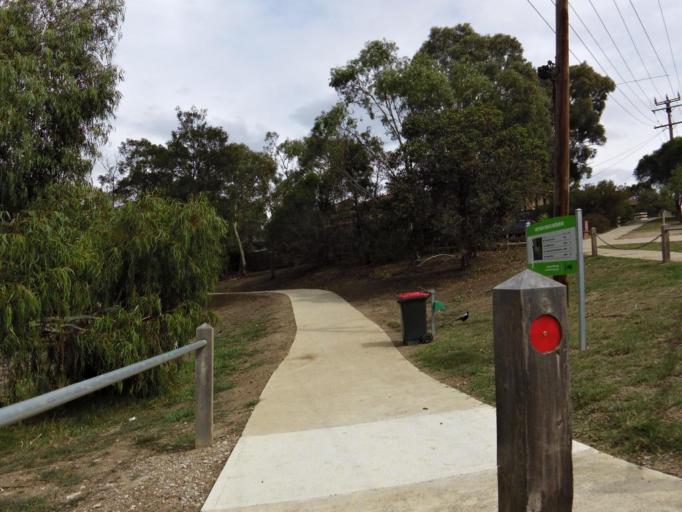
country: AU
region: Victoria
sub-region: Hume
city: Sunbury
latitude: -37.5725
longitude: 144.7138
